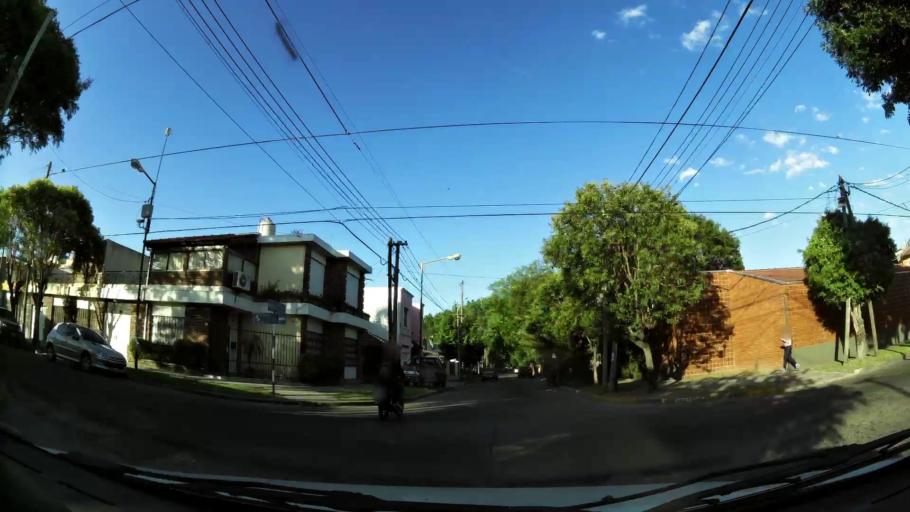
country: AR
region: Buenos Aires
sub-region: Partido de General San Martin
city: General San Martin
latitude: -34.5529
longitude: -58.5482
